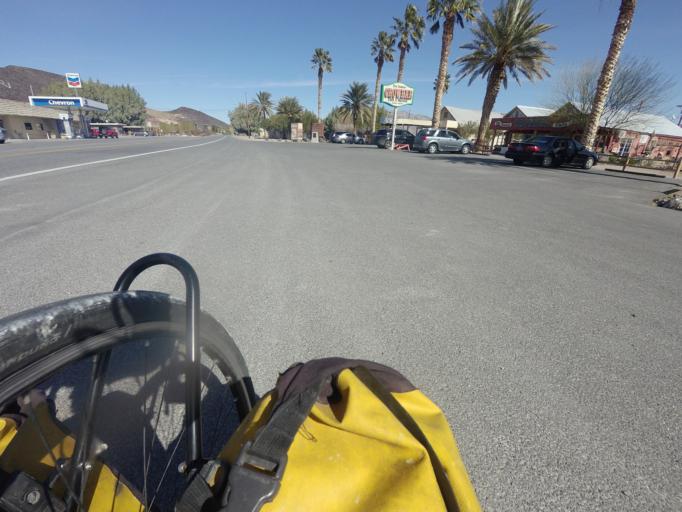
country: US
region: Nevada
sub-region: Nye County
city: Pahrump
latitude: 35.9745
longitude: -116.2702
